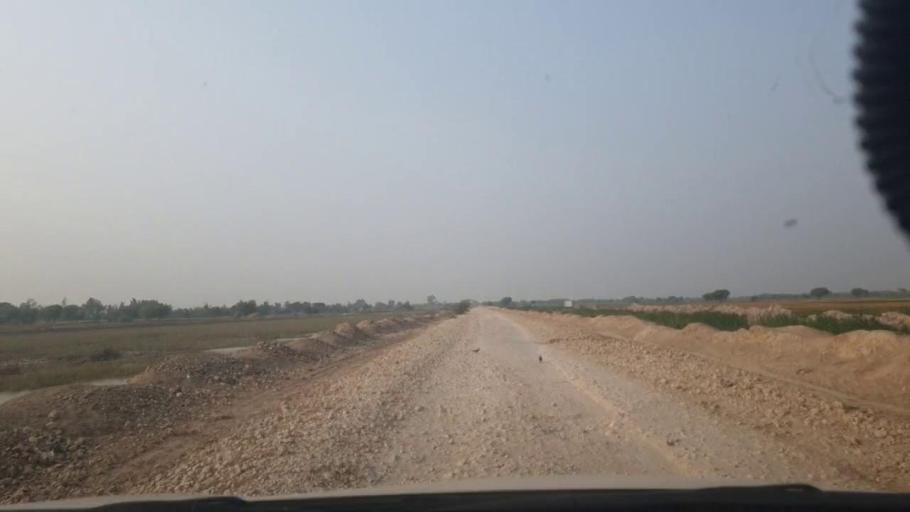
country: PK
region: Sindh
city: Bulri
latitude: 24.7922
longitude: 68.4179
